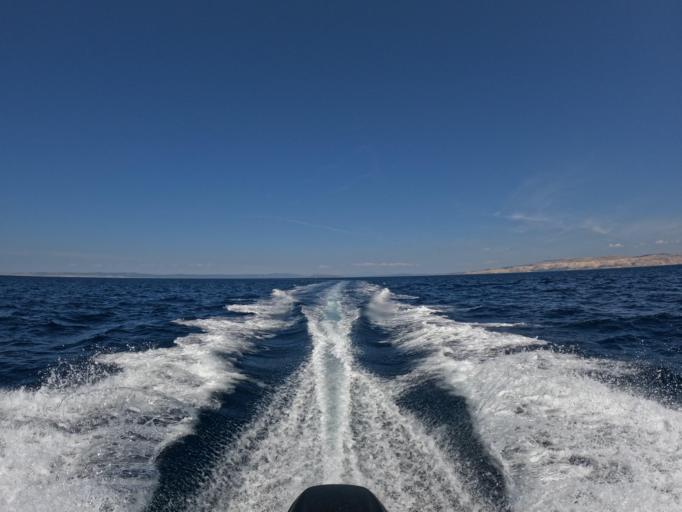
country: HR
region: Primorsko-Goranska
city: Lopar
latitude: 44.8586
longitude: 14.6947
